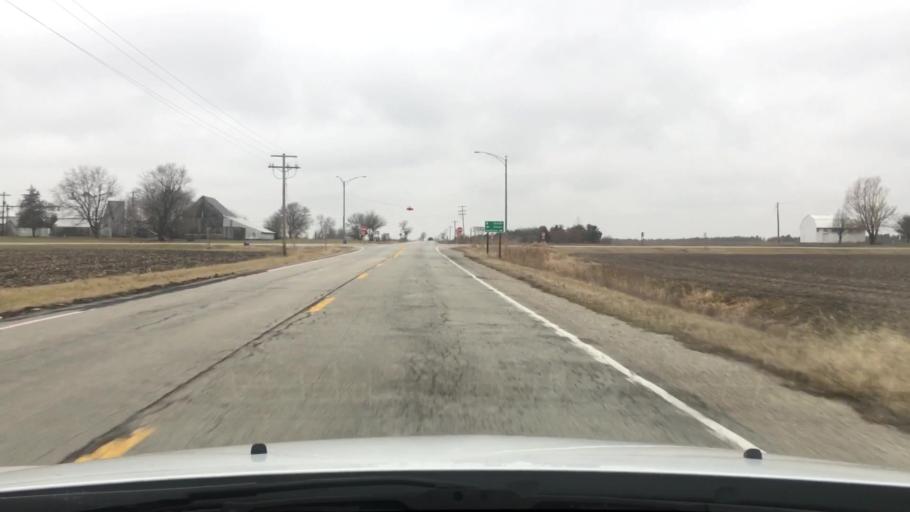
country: US
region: Illinois
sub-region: Iroquois County
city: Clifton
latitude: 40.8872
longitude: -87.8641
